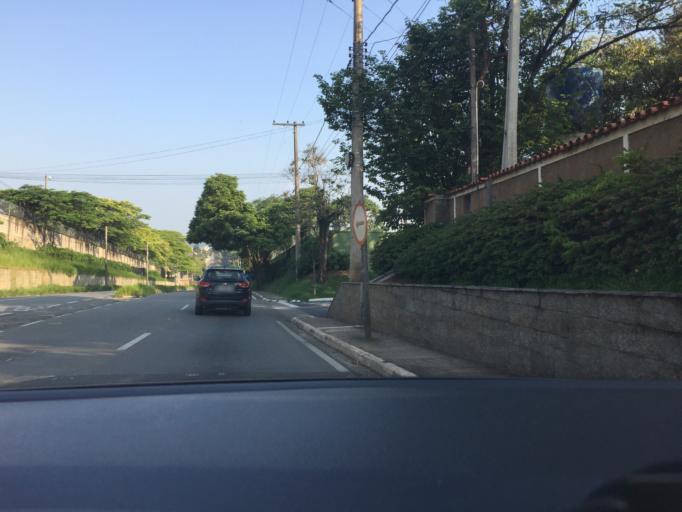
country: BR
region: Sao Paulo
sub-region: Vinhedo
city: Vinhedo
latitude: -23.0237
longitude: -46.9983
